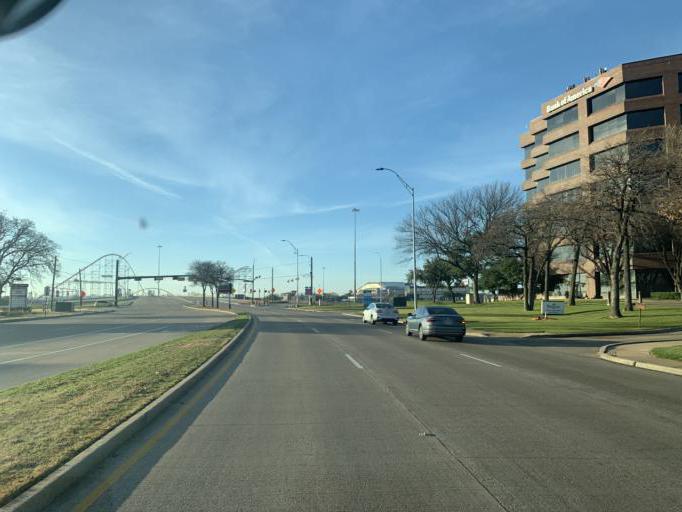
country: US
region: Texas
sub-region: Tarrant County
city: Arlington
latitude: 32.7623
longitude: -97.0759
